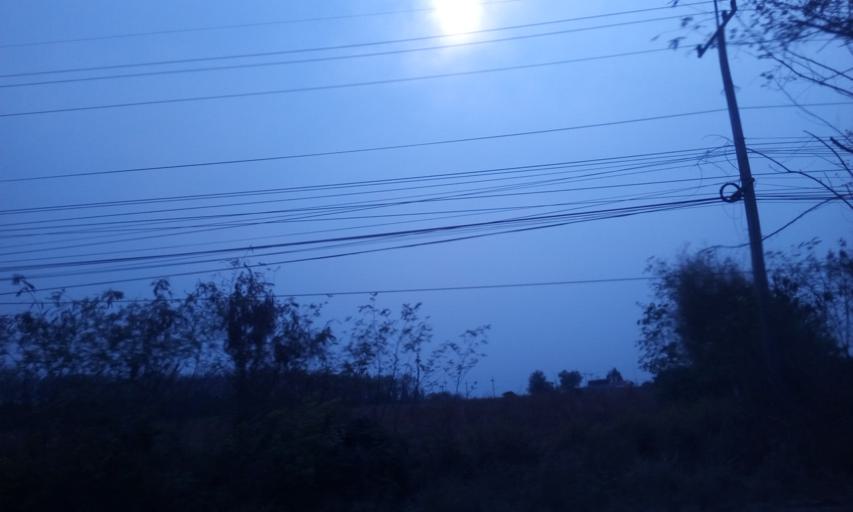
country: TH
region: Chachoengsao
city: Plaeng Yao
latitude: 13.5246
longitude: 101.2645
